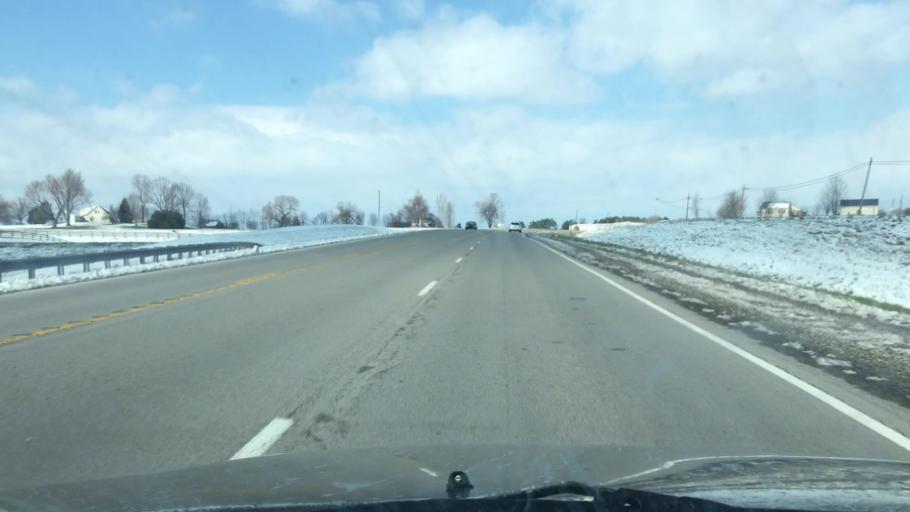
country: US
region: Kentucky
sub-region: Marion County
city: Lebanon
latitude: 37.5435
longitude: -85.3043
